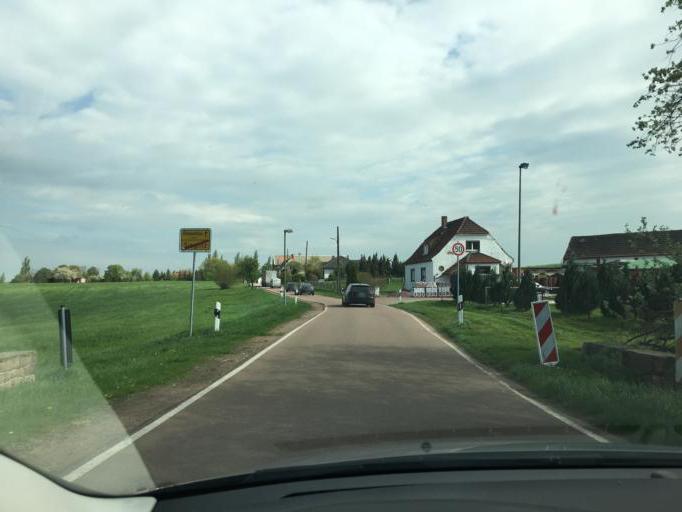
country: DE
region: Saxony-Anhalt
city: Grobzig
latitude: 51.6575
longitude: 11.8400
